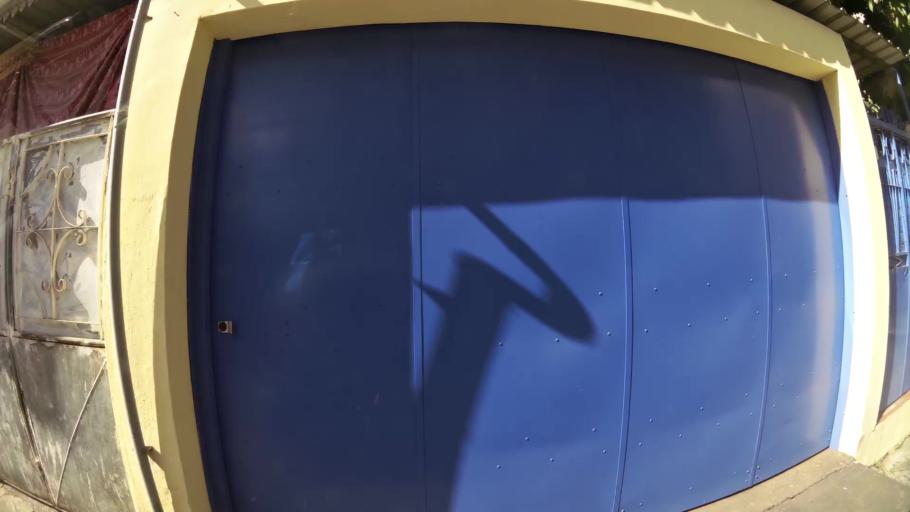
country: MU
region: Port Louis
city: Port Louis
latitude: -20.1608
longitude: 57.5173
